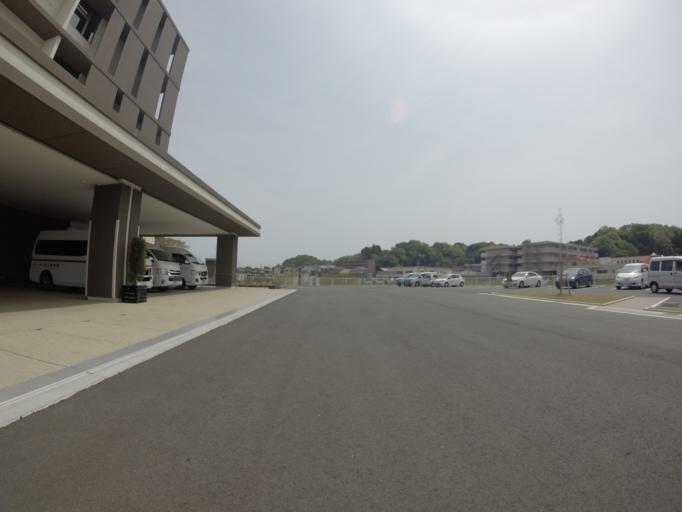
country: JP
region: Shizuoka
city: Kakegawa
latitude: 34.7616
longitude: 138.0271
